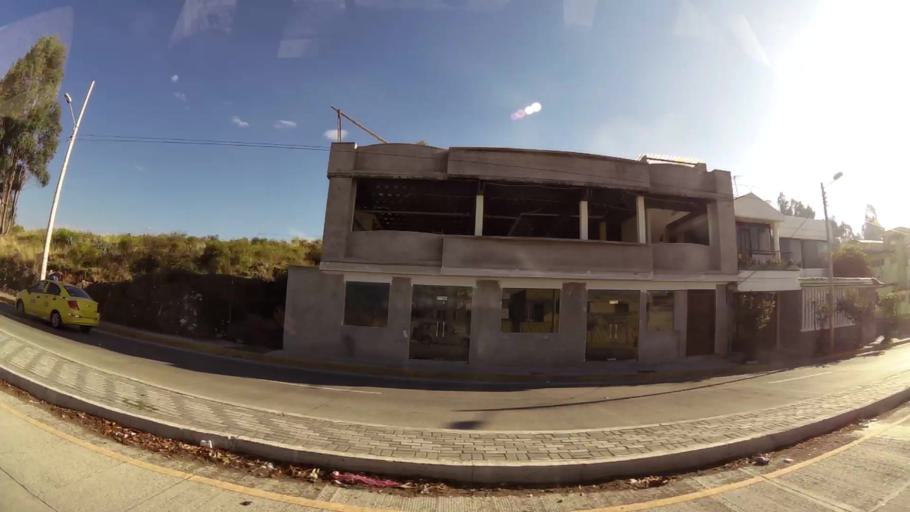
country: EC
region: Chimborazo
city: Riobamba
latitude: -1.6712
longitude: -78.6362
